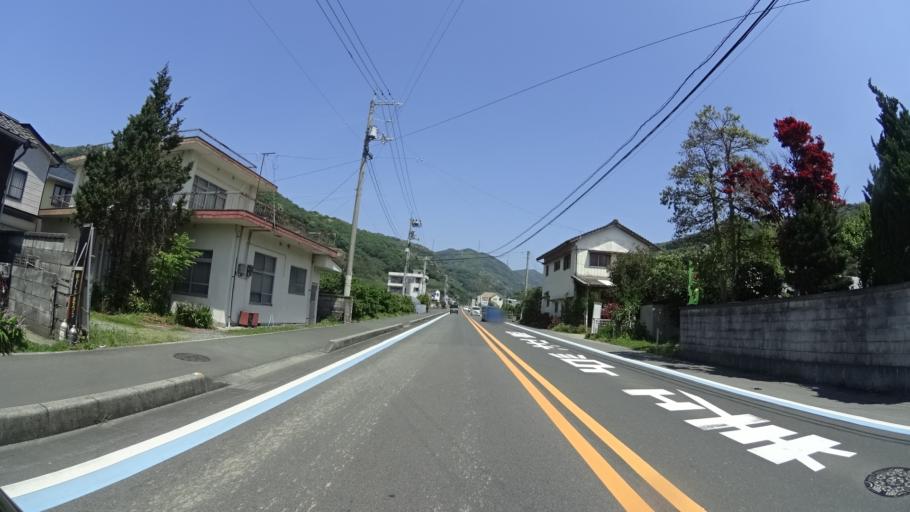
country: JP
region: Ehime
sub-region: Nishiuwa-gun
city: Ikata-cho
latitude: 33.4926
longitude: 132.3975
